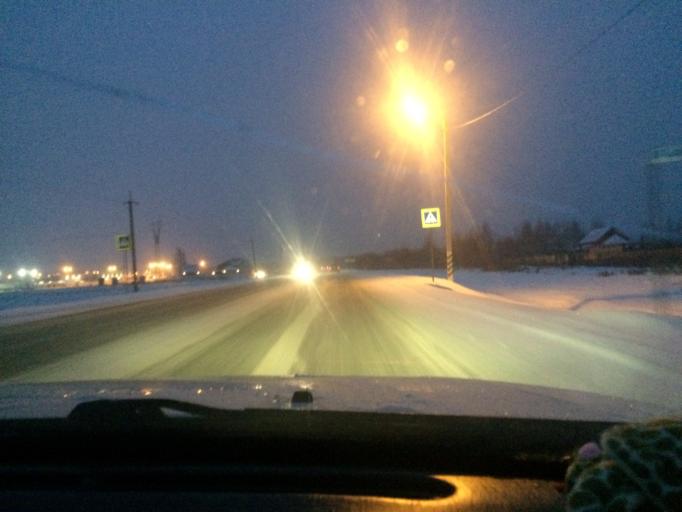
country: RU
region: Tula
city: Kosaya Gora
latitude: 54.1581
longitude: 37.4823
